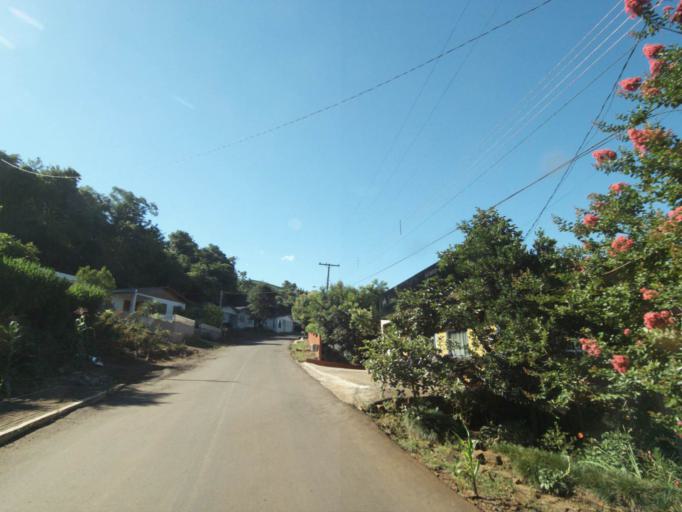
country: BR
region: Parana
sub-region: Ampere
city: Ampere
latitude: -26.1712
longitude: -53.3656
